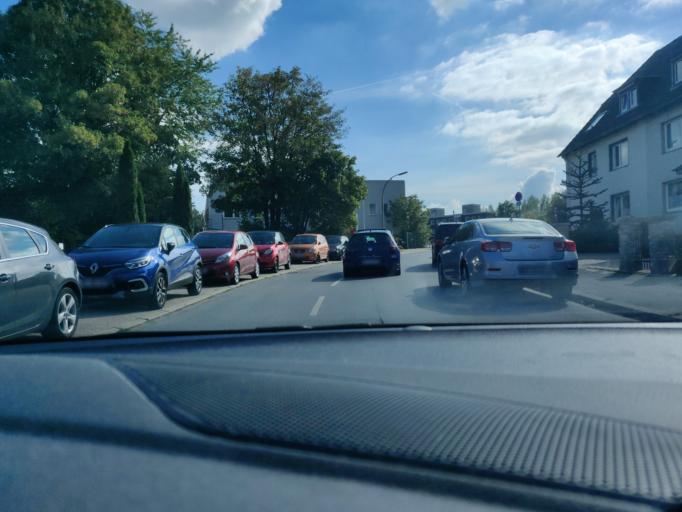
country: DE
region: North Rhine-Westphalia
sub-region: Regierungsbezirk Dusseldorf
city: Velbert
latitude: 51.3329
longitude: 7.0186
